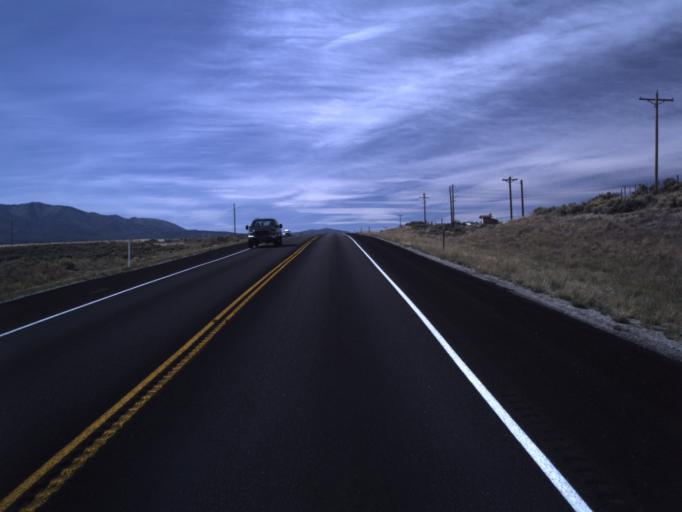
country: US
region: Utah
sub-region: San Juan County
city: Monticello
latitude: 37.8705
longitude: -109.2530
